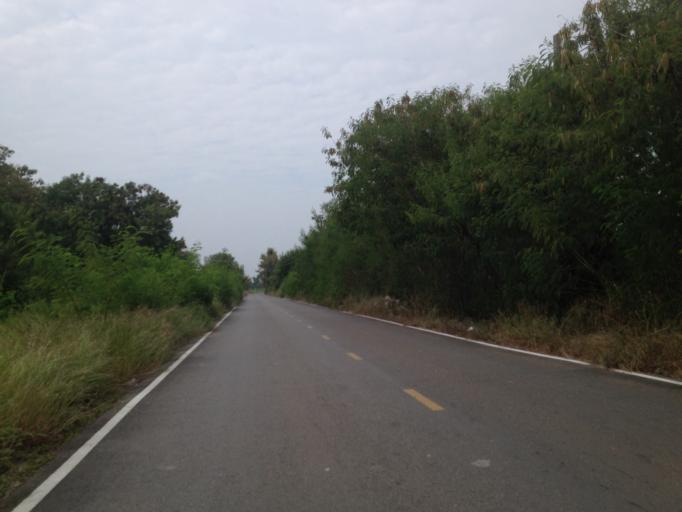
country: TH
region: Chiang Mai
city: San Pa Tong
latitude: 18.6559
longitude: 98.8989
